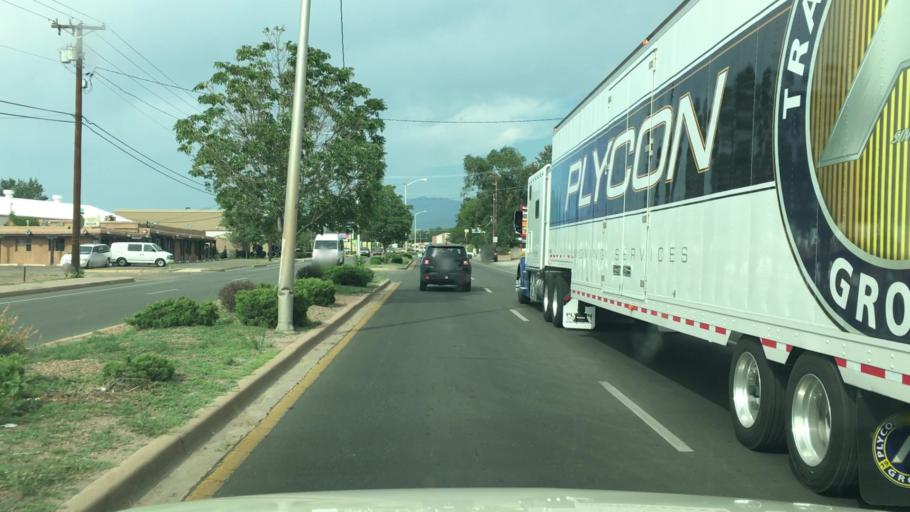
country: US
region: New Mexico
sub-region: Santa Fe County
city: Santa Fe
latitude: 35.6634
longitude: -105.9756
